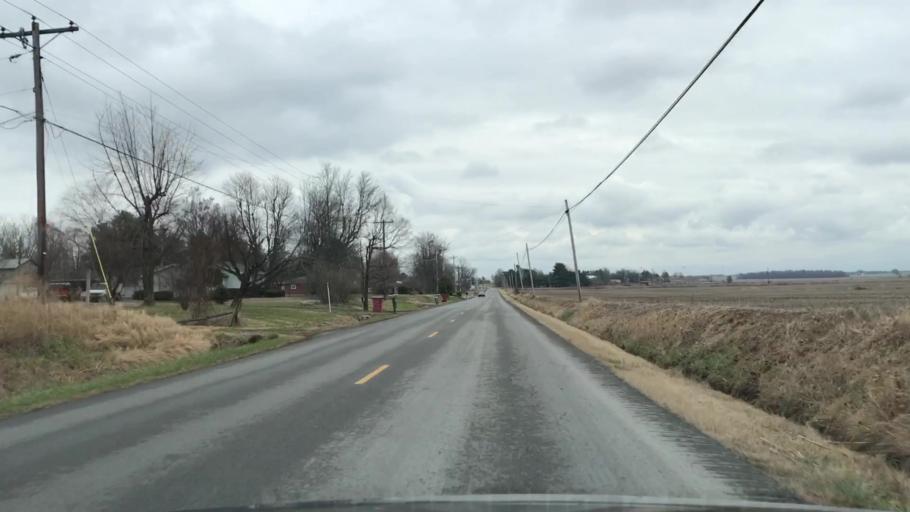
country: US
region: Kentucky
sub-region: McLean County
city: Calhoun
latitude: 37.5502
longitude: -87.2475
